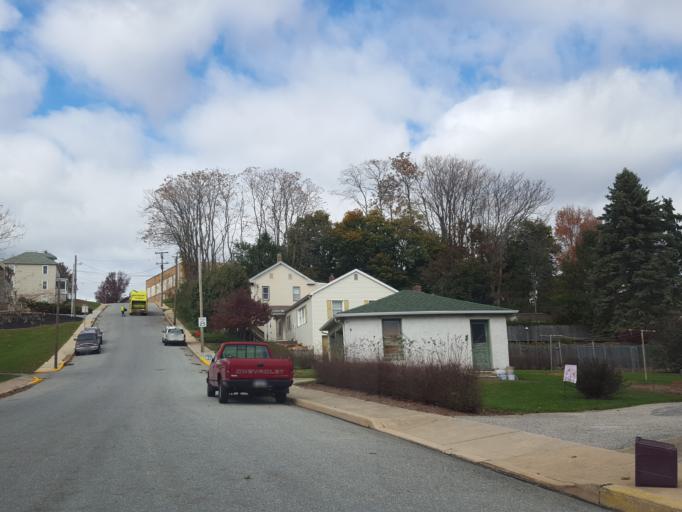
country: US
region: Pennsylvania
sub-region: York County
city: Red Lion
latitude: 39.8964
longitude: -76.6034
